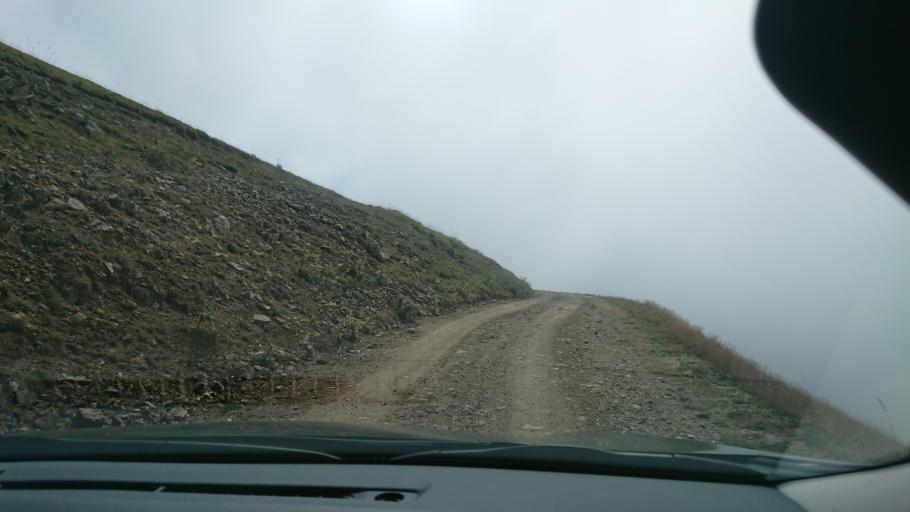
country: TR
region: Gumushane
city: Kurtun
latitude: 40.6250
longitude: 38.9934
